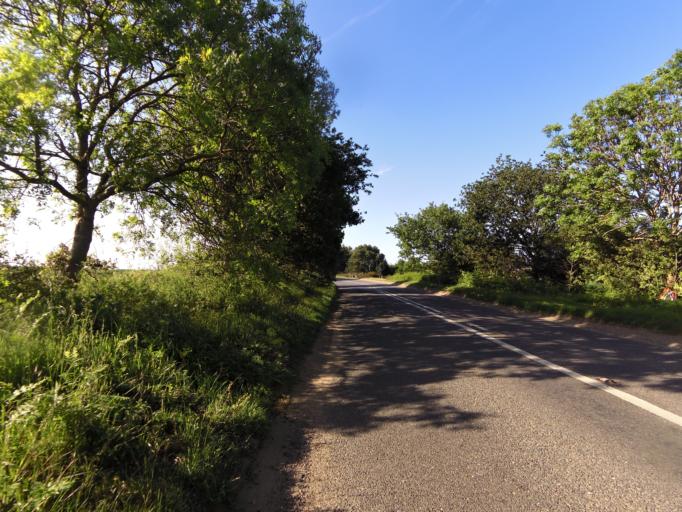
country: GB
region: England
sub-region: Suffolk
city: Woodbridge
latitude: 52.0772
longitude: 1.3636
